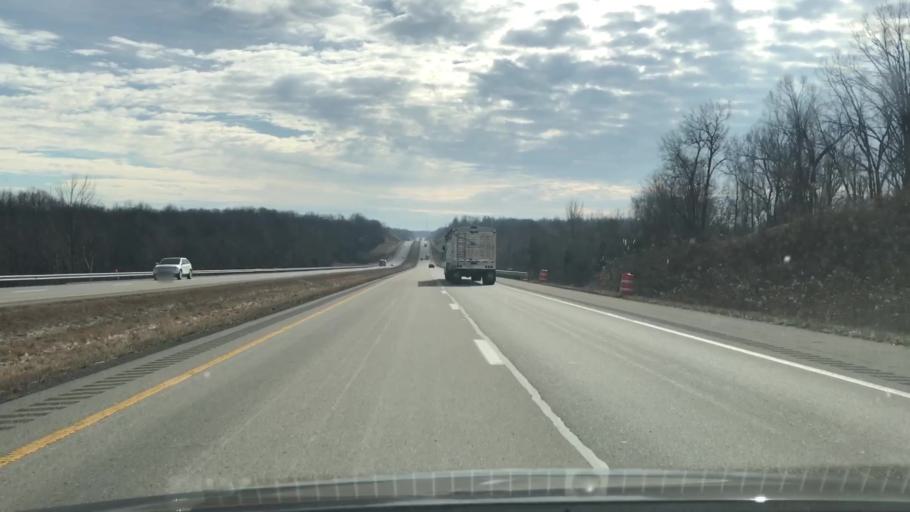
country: US
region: Kentucky
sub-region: Daviess County
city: Masonville
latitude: 37.5777
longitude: -86.9553
